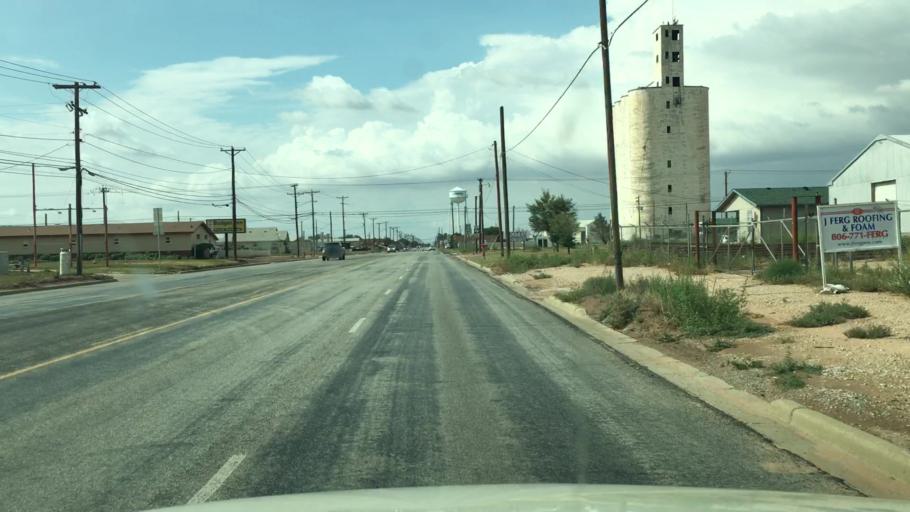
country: US
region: Texas
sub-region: Dawson County
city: Lamesa
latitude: 32.7251
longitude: -101.9467
